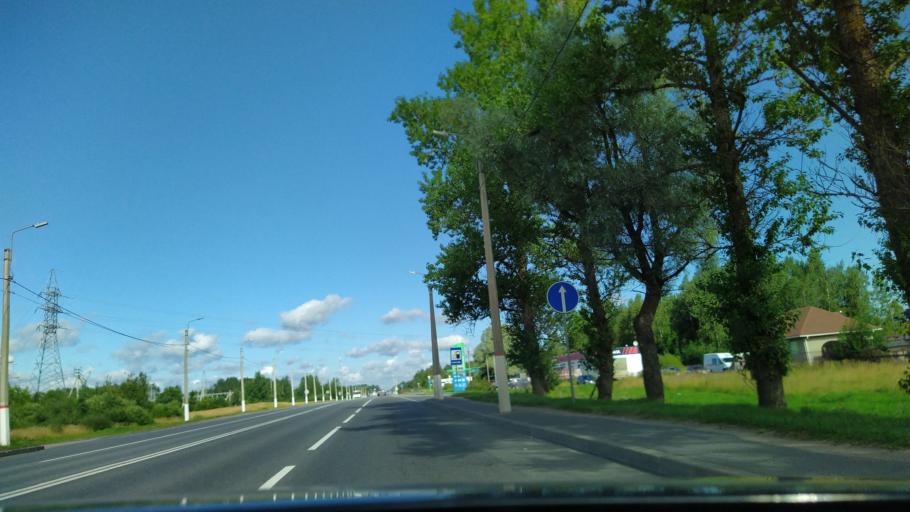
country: RU
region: Leningrad
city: Tosno
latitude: 59.5637
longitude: 30.8356
